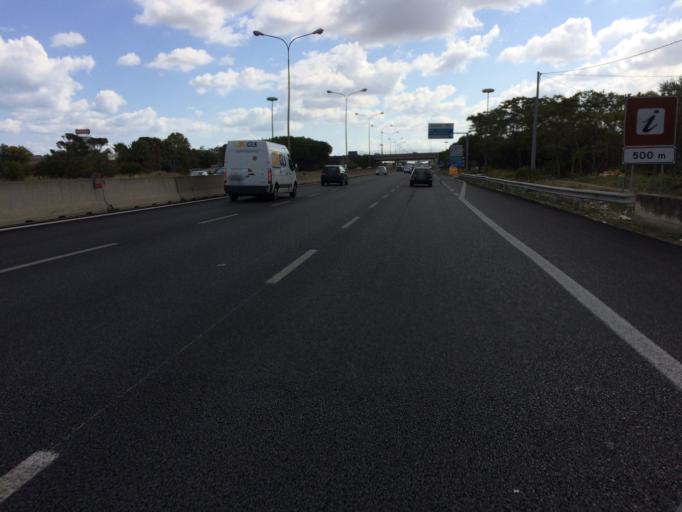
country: IT
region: Apulia
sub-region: Provincia di Bari
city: Bari
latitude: 41.0944
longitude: 16.8359
